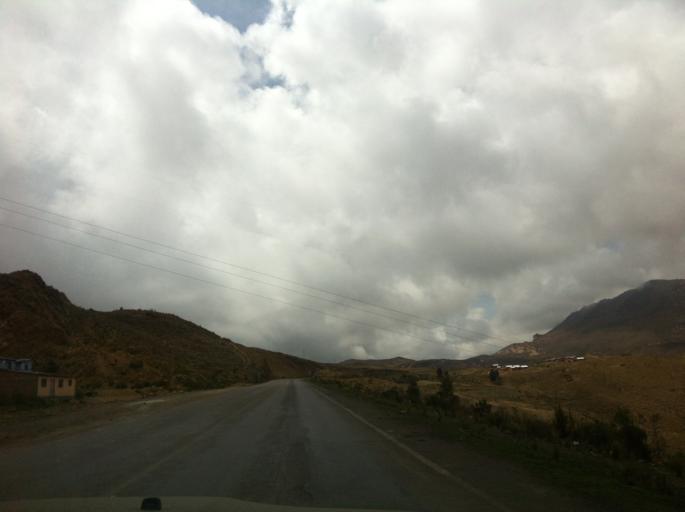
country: BO
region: Cochabamba
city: Irpa Irpa
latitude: -17.6755
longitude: -66.4845
